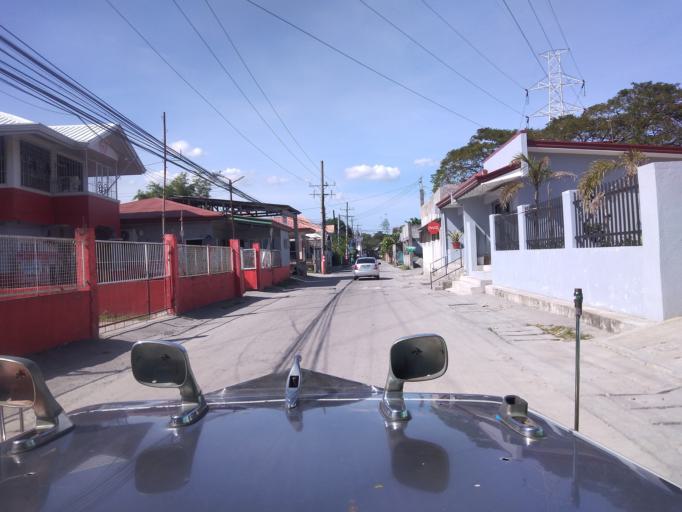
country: PH
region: Central Luzon
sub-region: Province of Pampanga
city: Magliman
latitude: 15.0291
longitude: 120.6680
